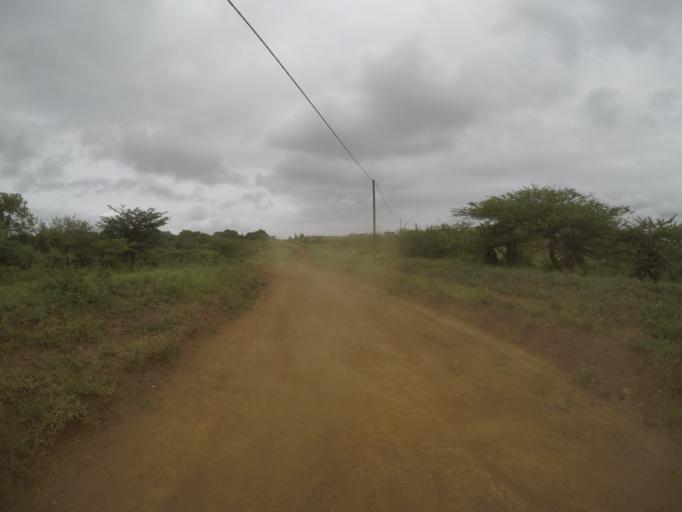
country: ZA
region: KwaZulu-Natal
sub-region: uThungulu District Municipality
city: Empangeni
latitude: -28.6022
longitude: 31.8457
